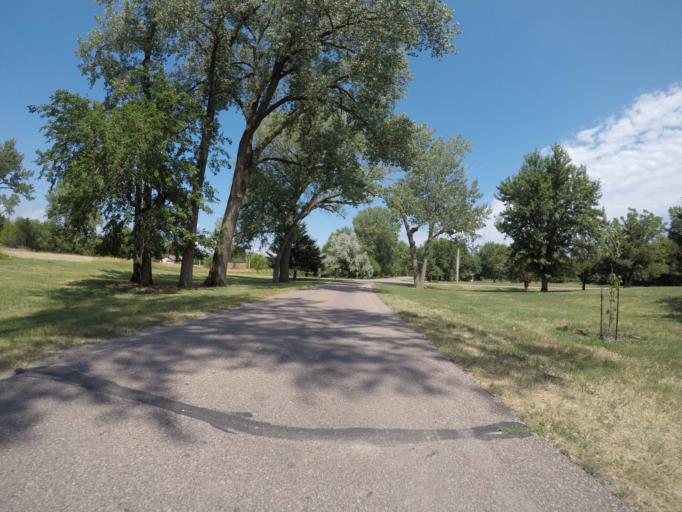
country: US
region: Nebraska
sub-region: Buffalo County
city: Kearney
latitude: 40.6552
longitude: -98.9901
